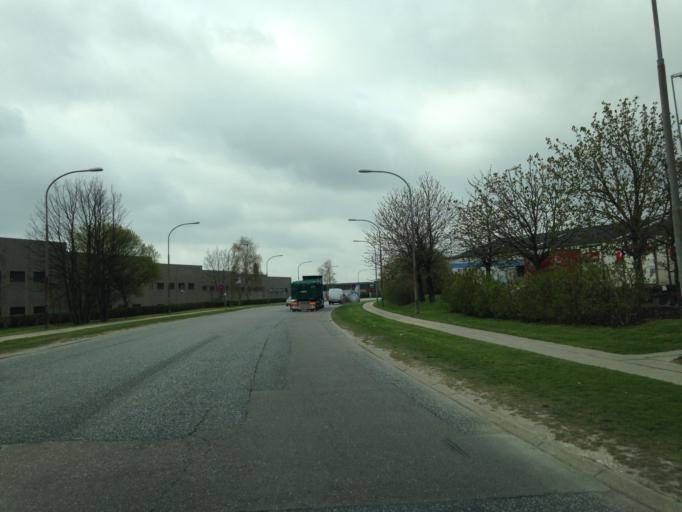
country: DK
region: Capital Region
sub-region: Ishoj Kommune
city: Ishoj
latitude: 55.6196
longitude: 12.3348
